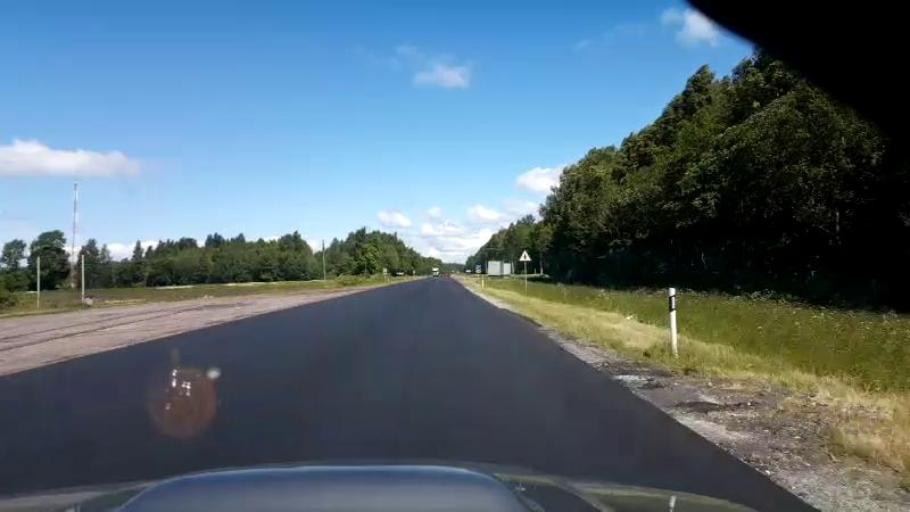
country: LV
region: Salacgrivas
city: Ainazi
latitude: 57.9693
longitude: 24.4498
